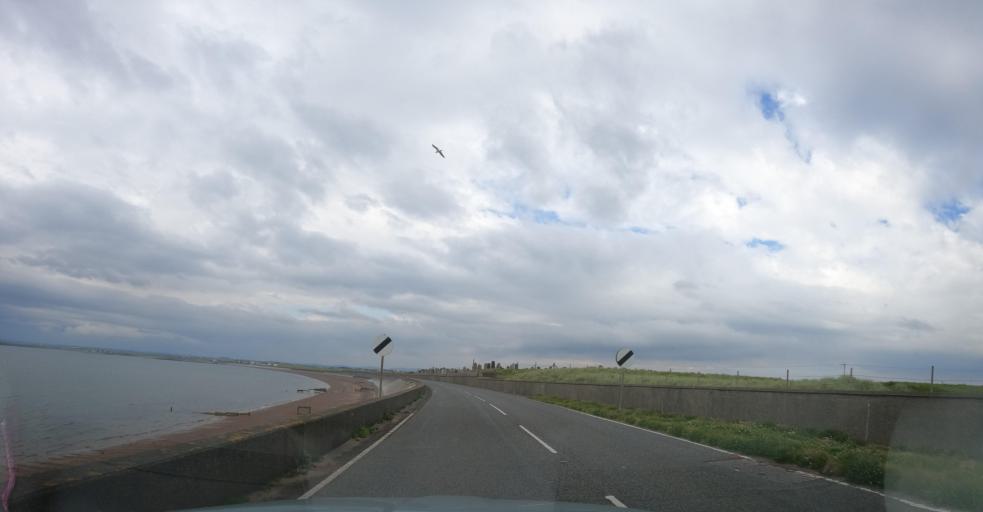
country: GB
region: Scotland
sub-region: Eilean Siar
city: Stornoway
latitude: 58.2054
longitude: -6.2862
